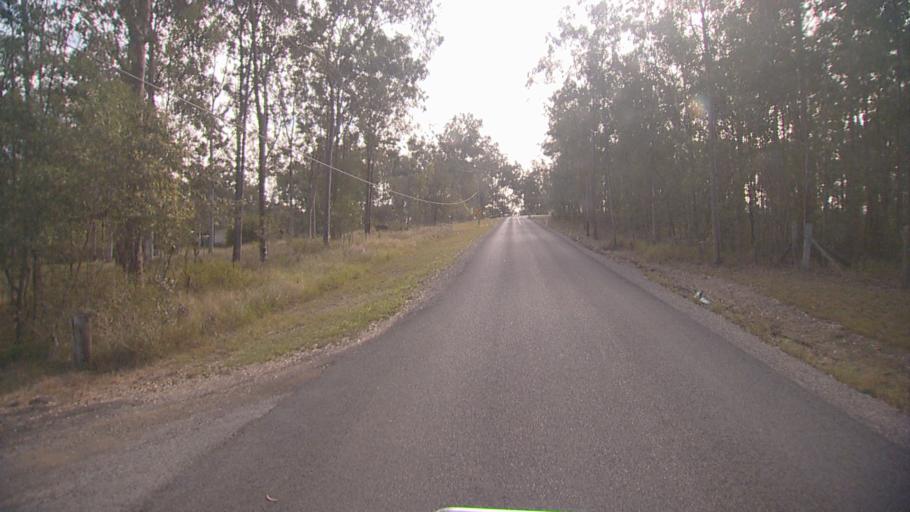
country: AU
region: Queensland
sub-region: Logan
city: North Maclean
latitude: -27.7721
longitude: 152.9654
